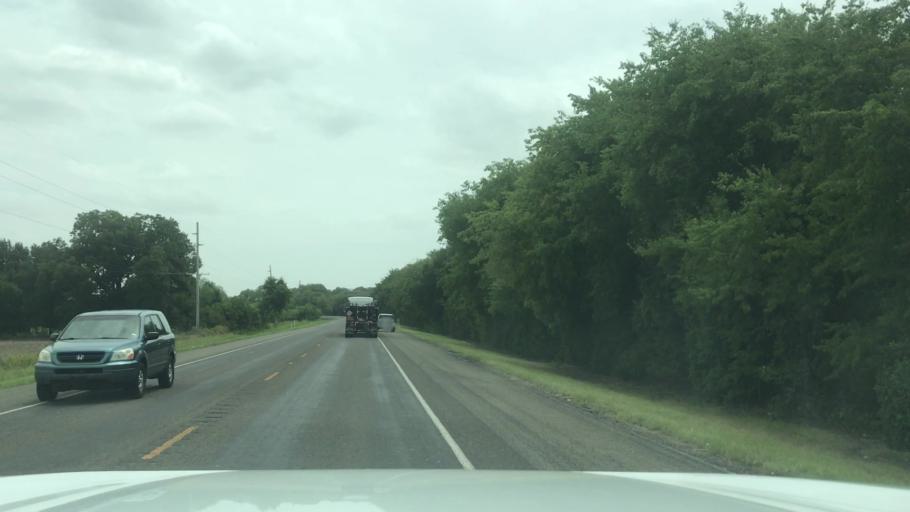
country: US
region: Texas
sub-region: Bosque County
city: Valley Mills
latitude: 31.6816
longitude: -97.5263
